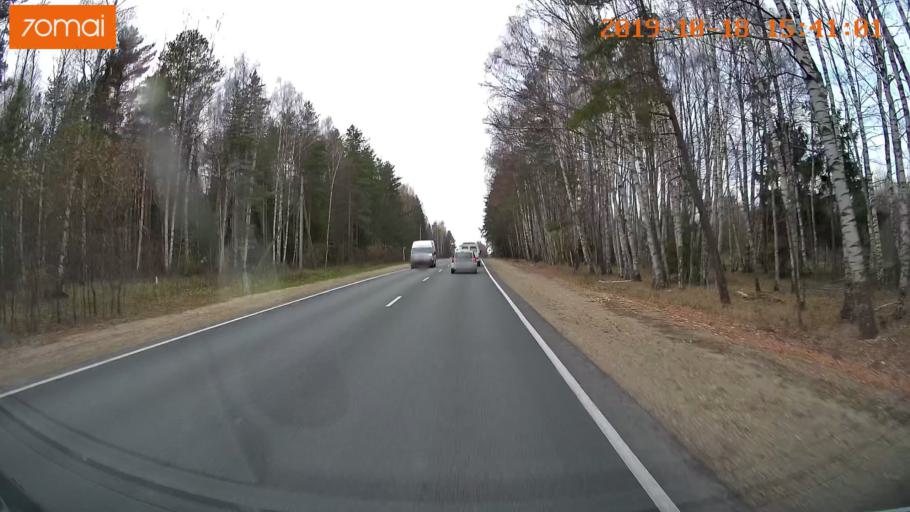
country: RU
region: Vladimir
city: Golovino
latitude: 55.9411
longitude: 40.5884
